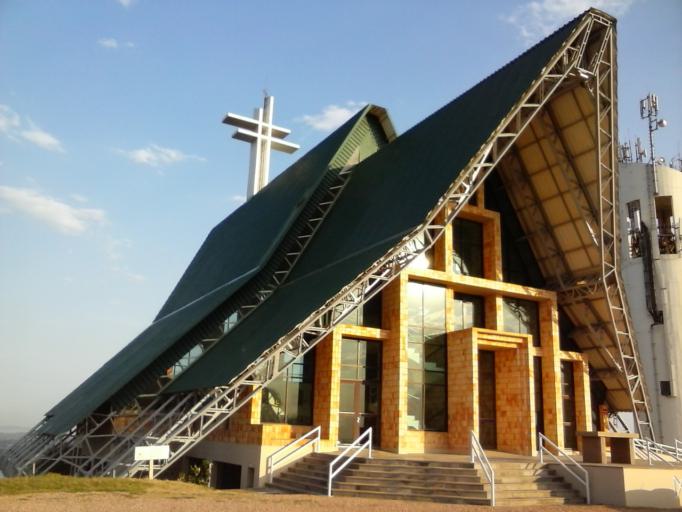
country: BR
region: Rio Grande do Sul
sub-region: Porto Alegre
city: Porto Alegre
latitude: -30.0995
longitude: -51.1818
